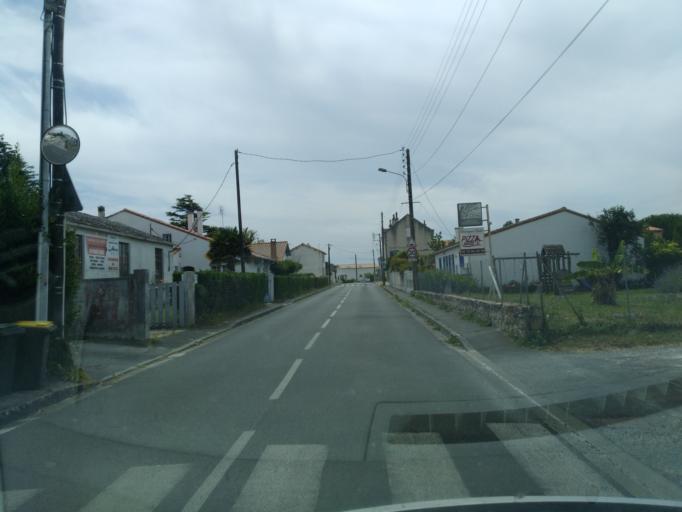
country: FR
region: Poitou-Charentes
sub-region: Departement de la Charente-Maritime
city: Saint-Palais-sur-Mer
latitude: 45.6562
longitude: -1.0775
